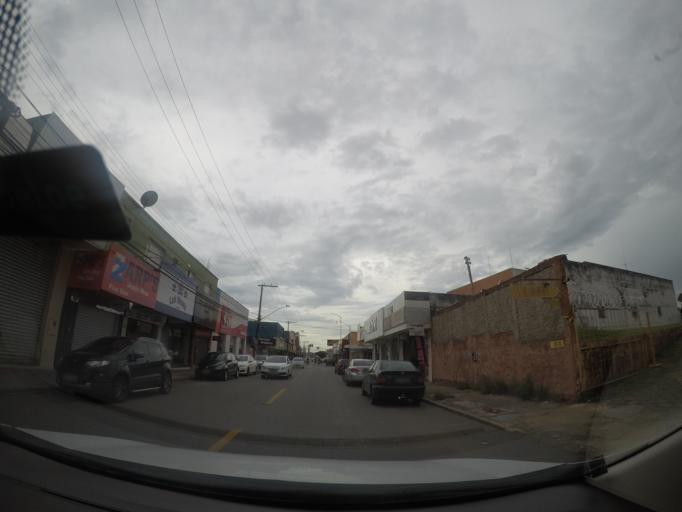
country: BR
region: Goias
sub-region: Goiania
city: Goiania
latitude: -16.6605
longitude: -49.2742
